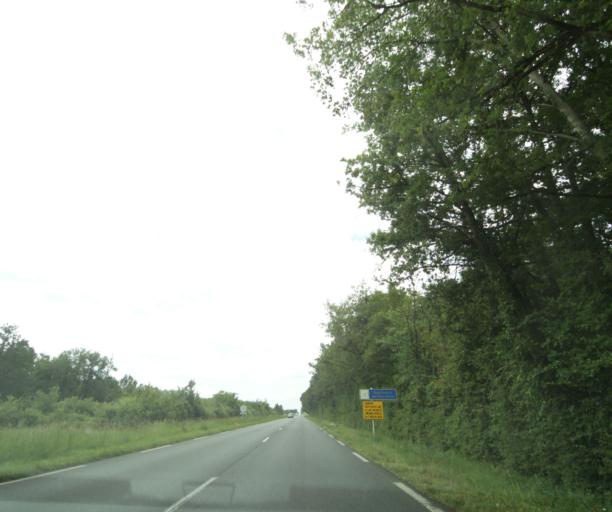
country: FR
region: Pays de la Loire
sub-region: Departement de Maine-et-Loire
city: Montreuil-Bellay
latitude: 47.1028
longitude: -0.1670
